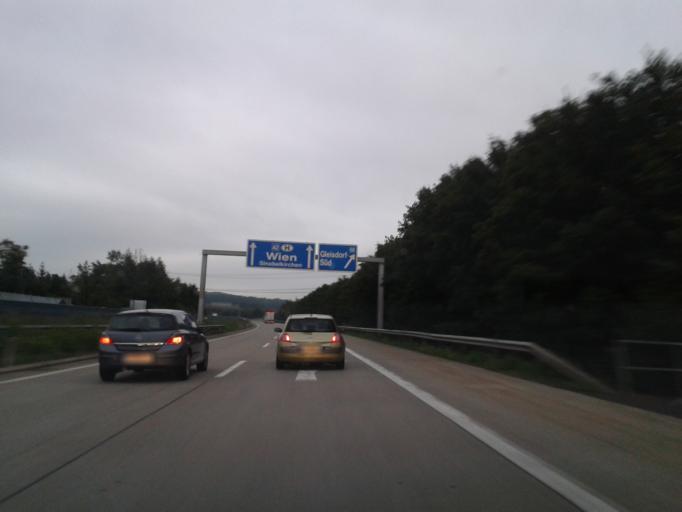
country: AT
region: Styria
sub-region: Politischer Bezirk Weiz
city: Gleisdorf
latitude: 47.0929
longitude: 15.7229
